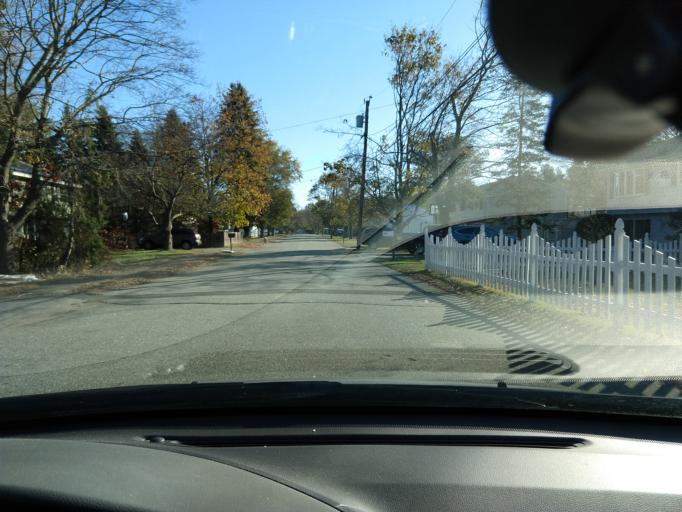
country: US
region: Massachusetts
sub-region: Middlesex County
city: Bedford
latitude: 42.4722
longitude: -71.2713
